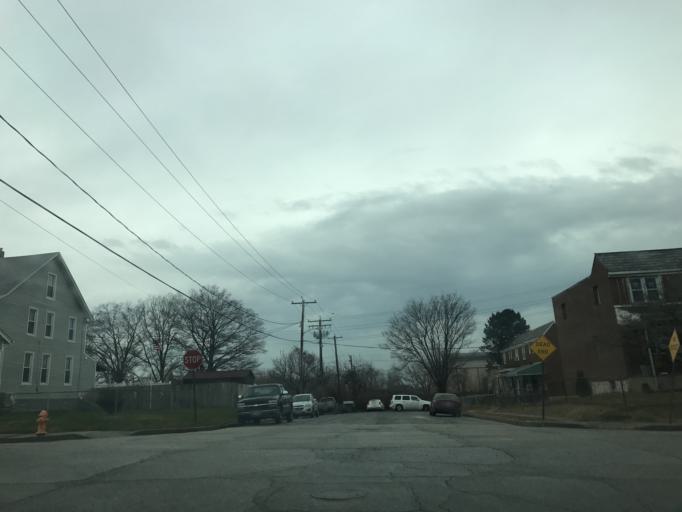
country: US
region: Maryland
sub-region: Baltimore County
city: Rosedale
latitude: 39.3031
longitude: -76.5624
